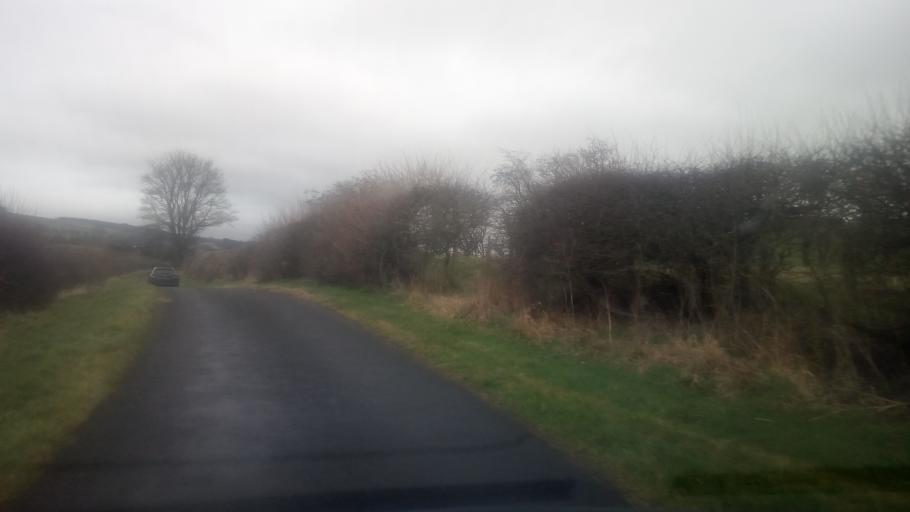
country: GB
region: Scotland
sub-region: The Scottish Borders
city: Jedburgh
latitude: 55.5004
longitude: -2.5390
